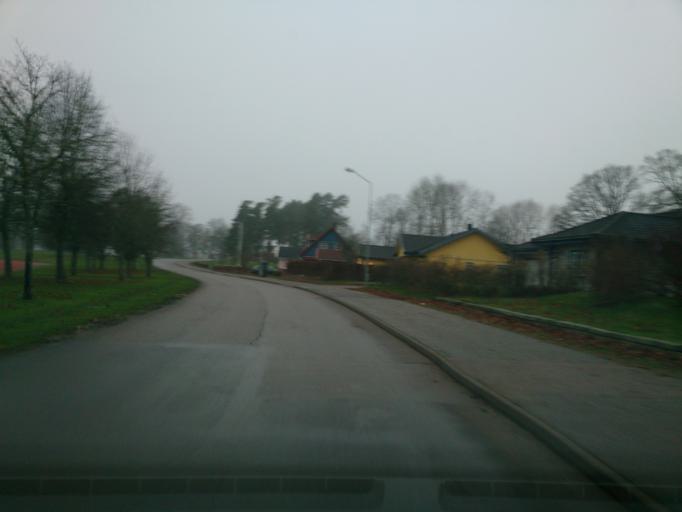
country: SE
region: OEstergoetland
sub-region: Atvidabergs Kommun
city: Atvidaberg
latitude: 58.1916
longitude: 16.0008
